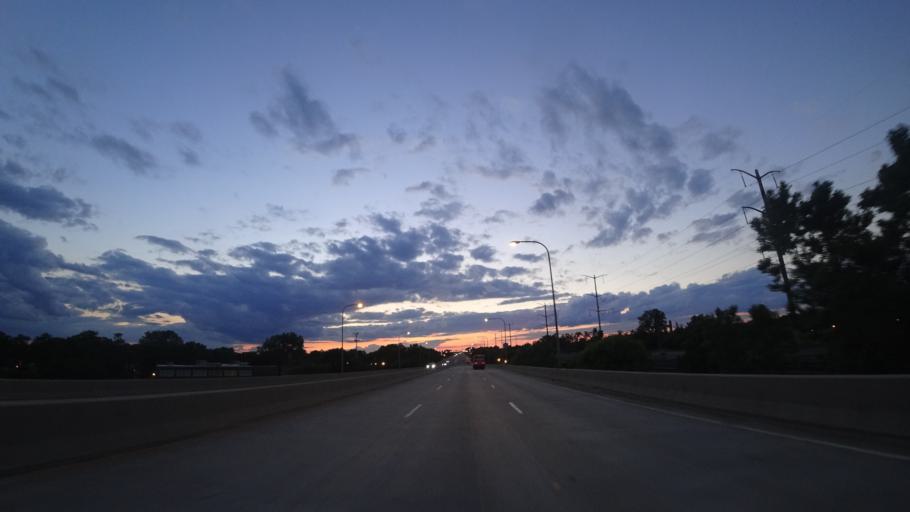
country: US
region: Illinois
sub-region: Cook County
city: Chicago
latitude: 41.7575
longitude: -87.5964
